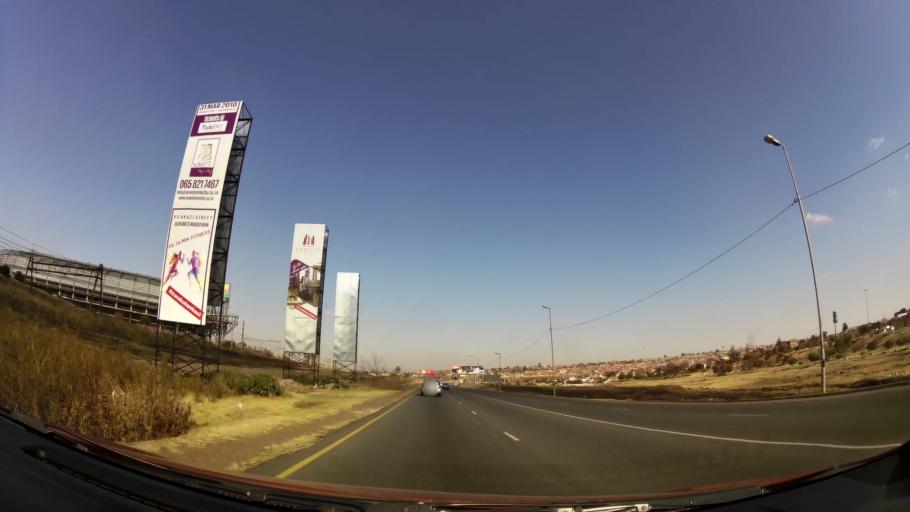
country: ZA
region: Gauteng
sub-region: City of Johannesburg Metropolitan Municipality
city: Soweto
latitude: -26.2290
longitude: 27.9232
